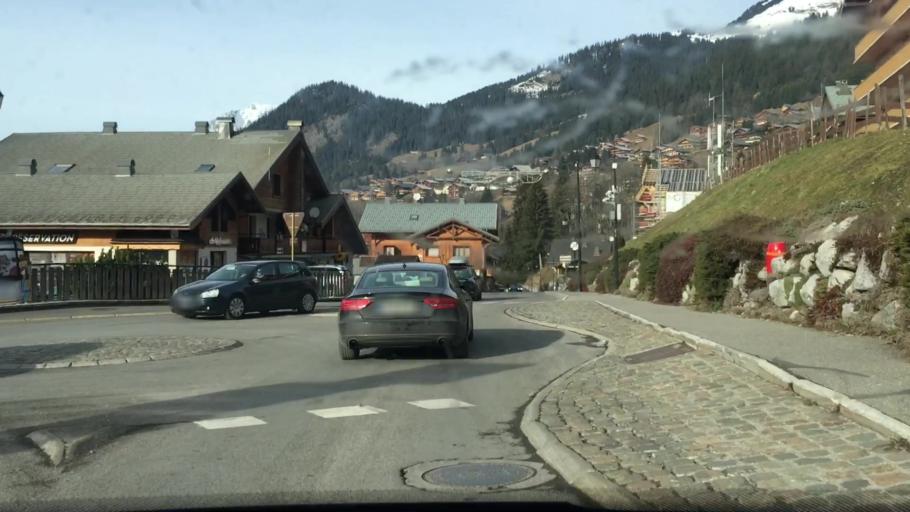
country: FR
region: Rhone-Alpes
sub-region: Departement de la Haute-Savoie
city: Chatel
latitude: 46.2692
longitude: 6.8406
